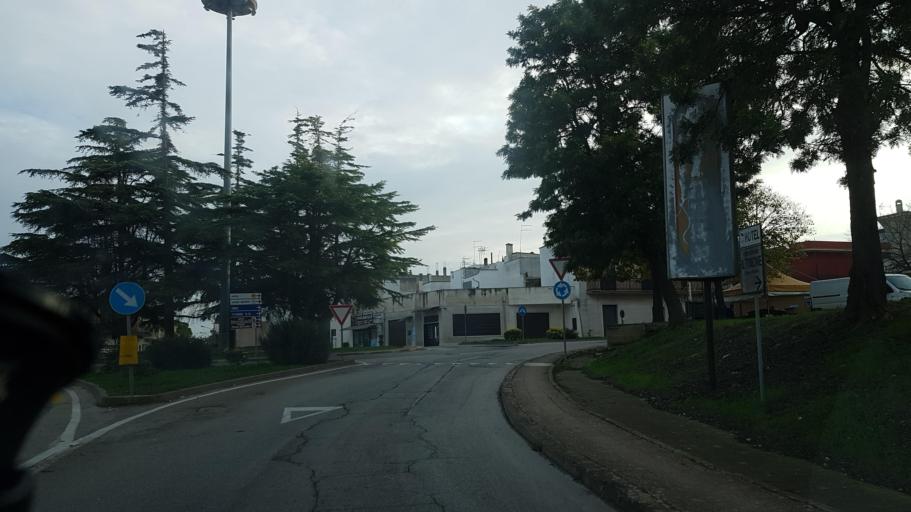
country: IT
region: Apulia
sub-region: Provincia di Brindisi
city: Latiano
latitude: 40.5571
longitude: 17.7156
